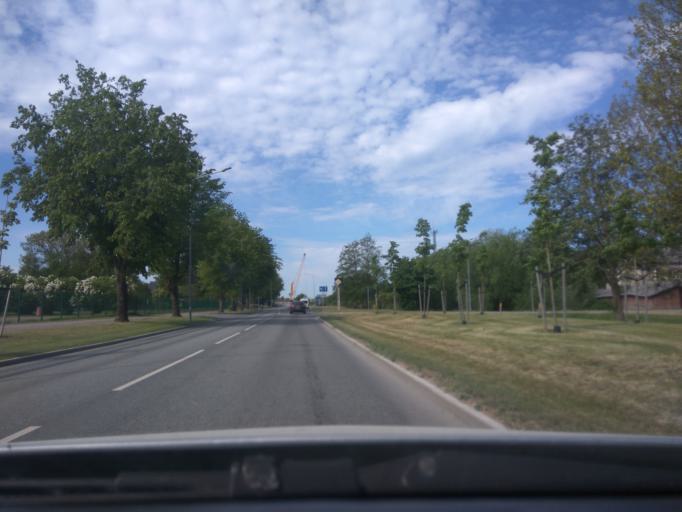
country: LV
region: Ventspils
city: Ventspils
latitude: 57.3917
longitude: 21.5984
